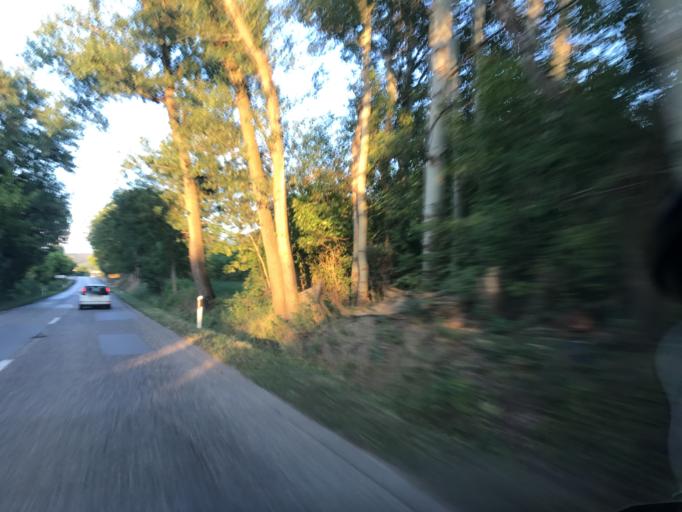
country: RS
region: Central Serbia
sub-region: Branicevski Okrug
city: Veliko Gradiste
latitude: 44.7202
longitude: 21.4250
